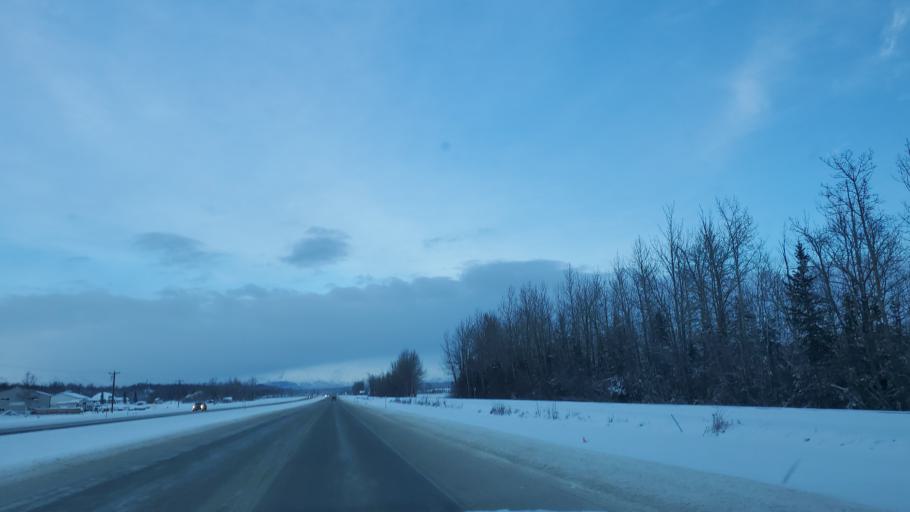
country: US
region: Alaska
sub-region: Matanuska-Susitna Borough
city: Palmer
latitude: 61.5725
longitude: -149.1475
